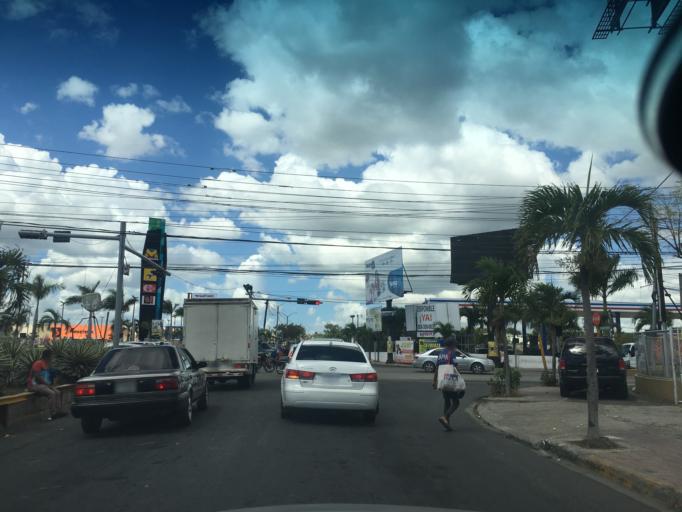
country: DO
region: La Romana
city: La Romana
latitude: 18.4320
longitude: -68.9918
